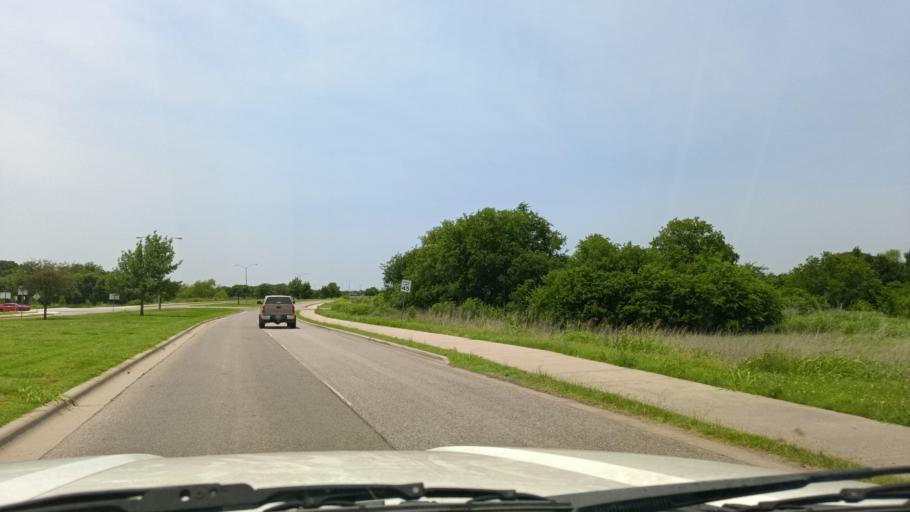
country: US
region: Texas
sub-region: Bell County
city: Temple
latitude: 31.1291
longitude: -97.4001
